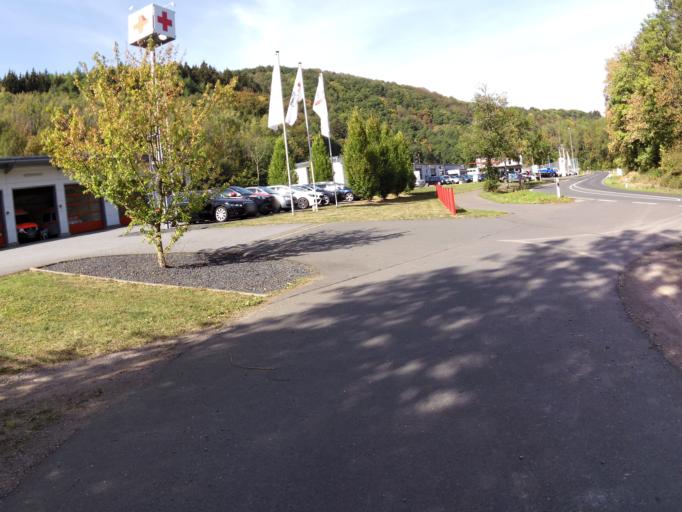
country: DE
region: Rheinland-Pfalz
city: Scheuern
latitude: 50.0020
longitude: 6.3039
